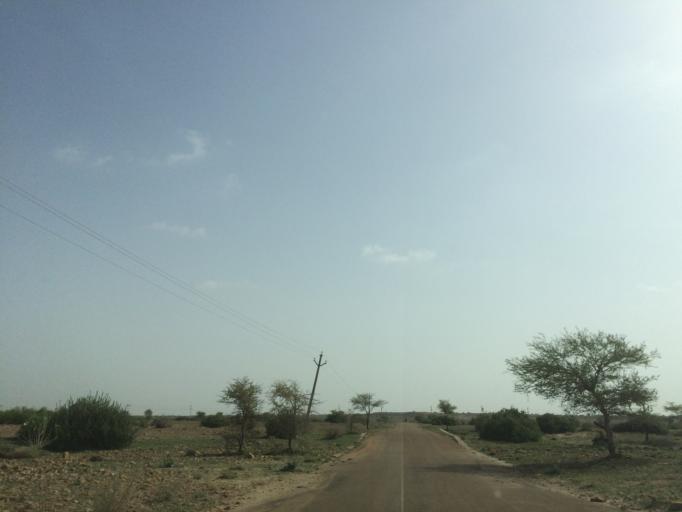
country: IN
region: Rajasthan
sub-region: Jaisalmer
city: Jaisalmer
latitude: 26.8362
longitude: 70.7430
